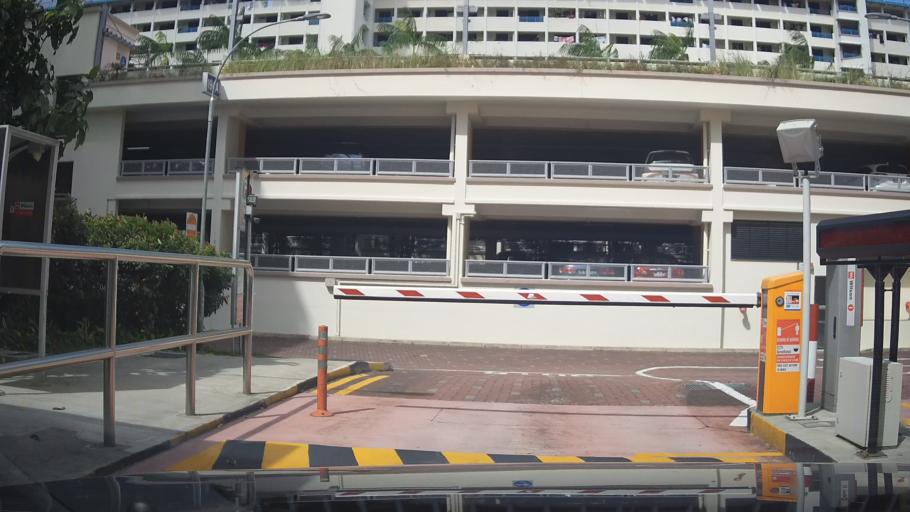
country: SG
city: Singapore
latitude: 1.3311
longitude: 103.8590
